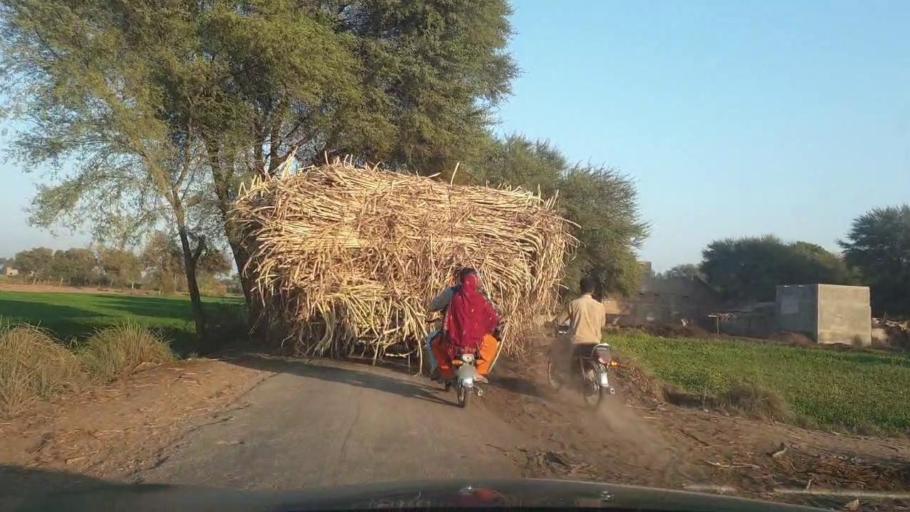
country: PK
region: Sindh
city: Ubauro
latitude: 28.1707
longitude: 69.5940
